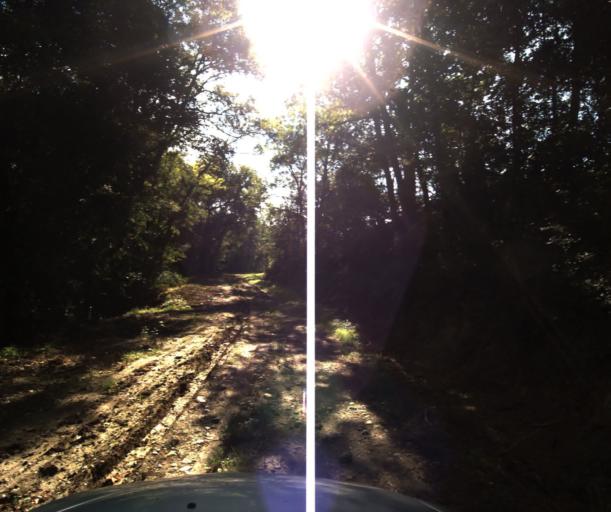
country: FR
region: Midi-Pyrenees
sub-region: Departement de la Haute-Garonne
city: Vieille-Toulouse
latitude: 43.5174
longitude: 1.4260
